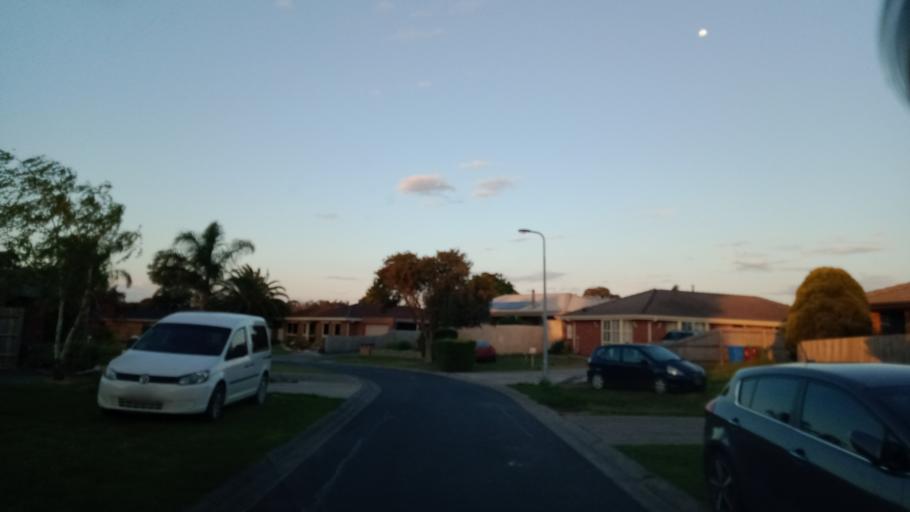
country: AU
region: Victoria
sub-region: Casey
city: Cranbourne North
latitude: -38.0828
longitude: 145.2687
